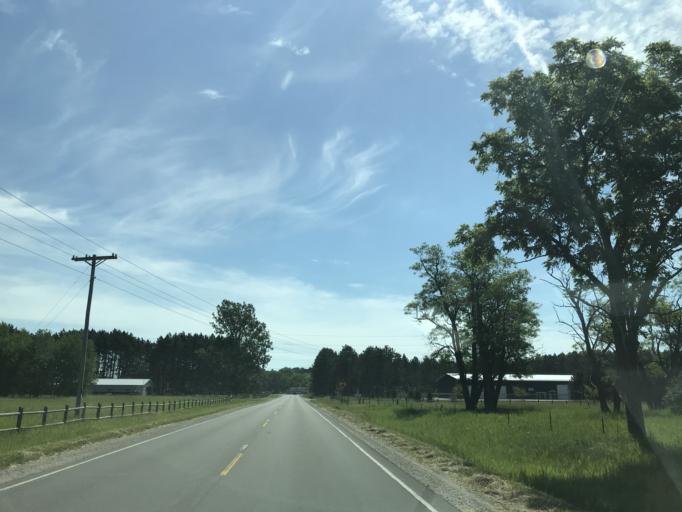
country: US
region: Michigan
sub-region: Grand Traverse County
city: Traverse City
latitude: 44.6541
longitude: -85.7007
